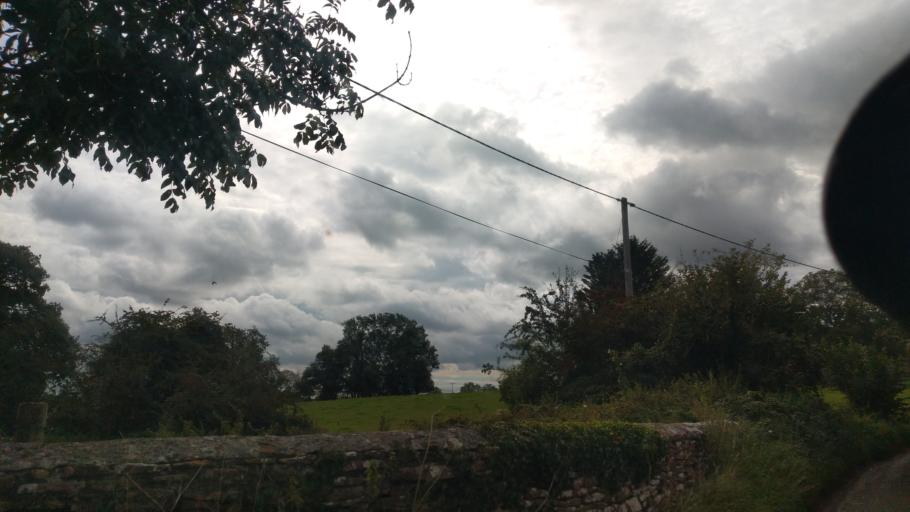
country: GB
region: England
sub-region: Wiltshire
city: Corsham
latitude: 51.4331
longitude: -2.1653
